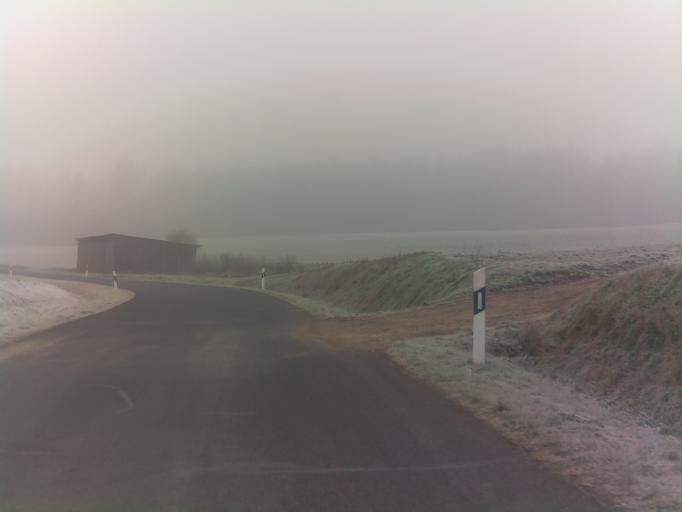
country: DE
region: Bavaria
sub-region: Regierungsbezirk Unterfranken
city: Burgpreppach
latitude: 50.1222
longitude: 10.6254
